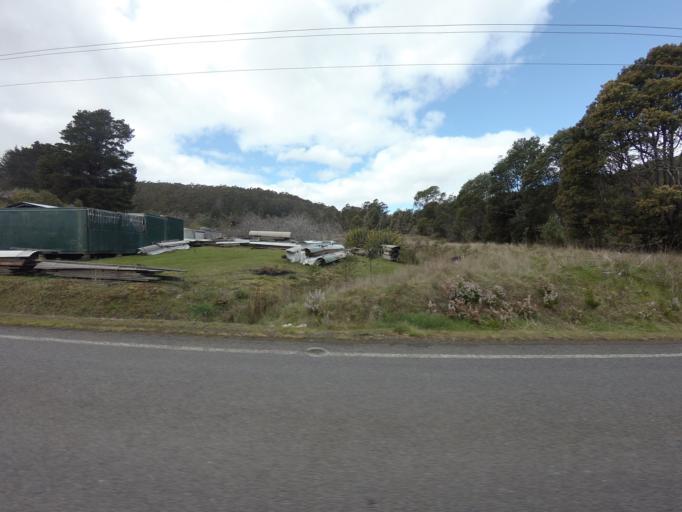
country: AU
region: Tasmania
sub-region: Huon Valley
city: Cygnet
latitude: -43.2697
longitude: 147.0105
